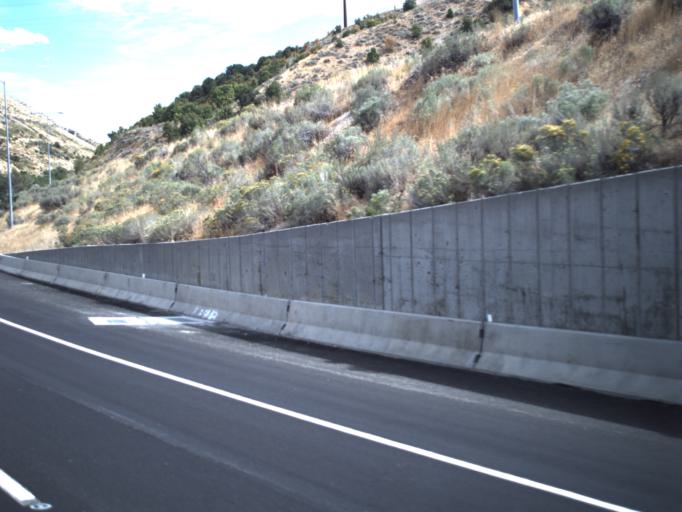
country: US
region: Utah
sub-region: Box Elder County
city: Brigham City
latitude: 41.4996
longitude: -111.9916
